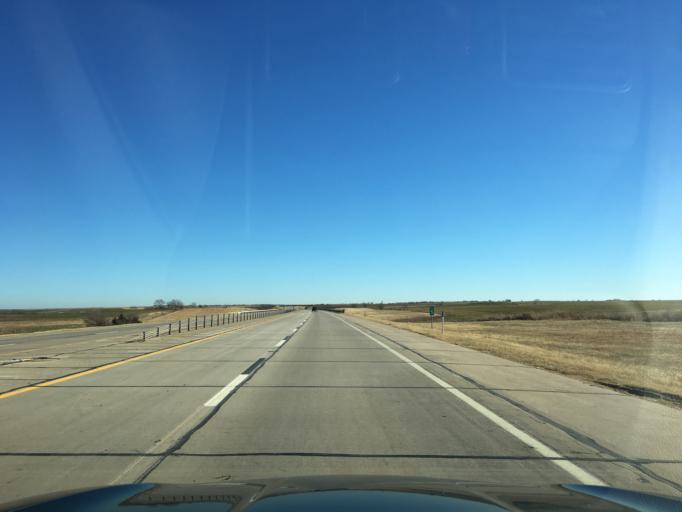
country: US
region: Oklahoma
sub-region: Noble County
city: Perry
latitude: 36.3992
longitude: -97.2396
